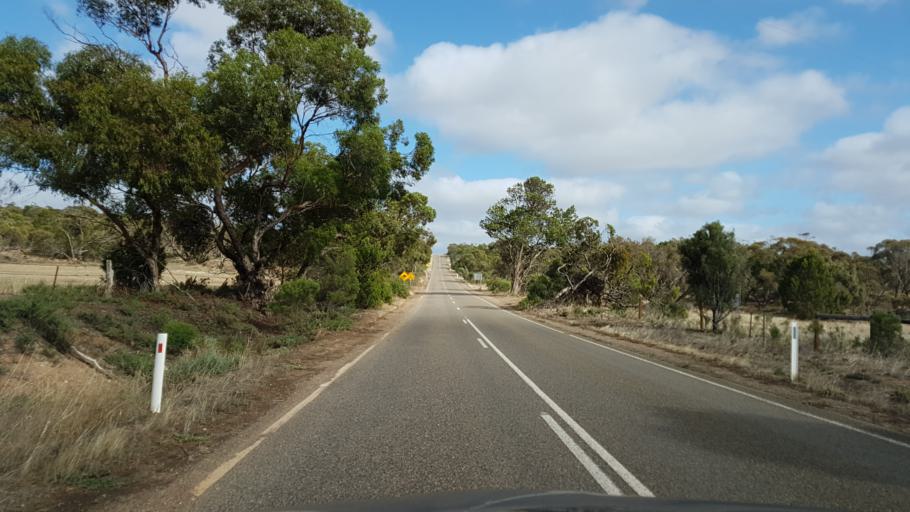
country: AU
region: South Australia
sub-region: Murray Bridge
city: Murray Bridge
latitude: -35.1155
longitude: 139.2311
